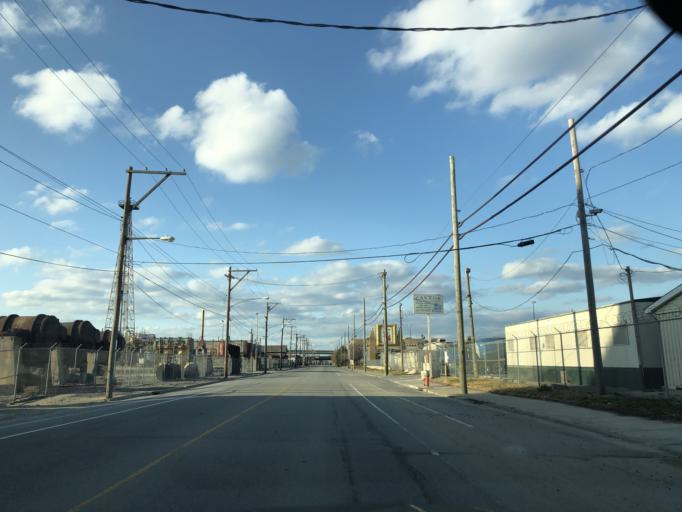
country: US
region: New Jersey
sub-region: Camden County
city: Pennsauken
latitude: 39.9840
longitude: -75.0851
